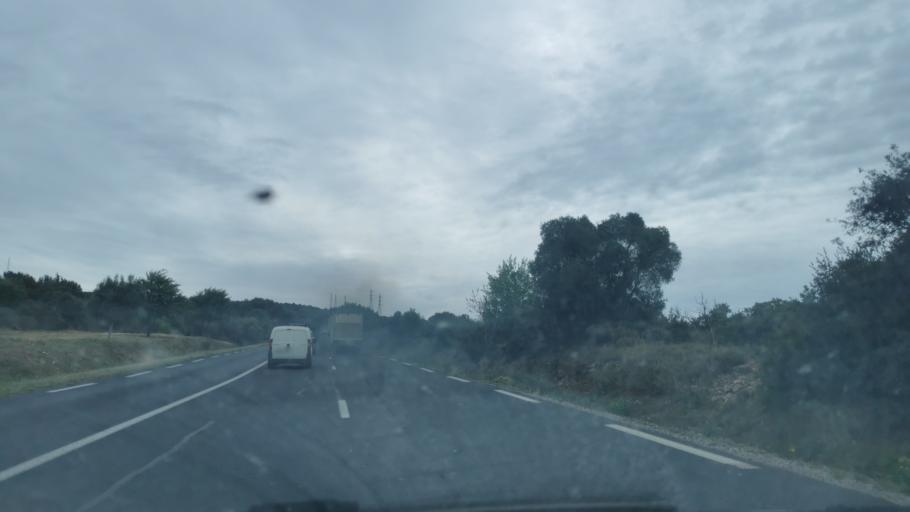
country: FR
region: Languedoc-Roussillon
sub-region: Departement de l'Herault
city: Balaruc-le-Vieux
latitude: 43.4582
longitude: 3.6974
